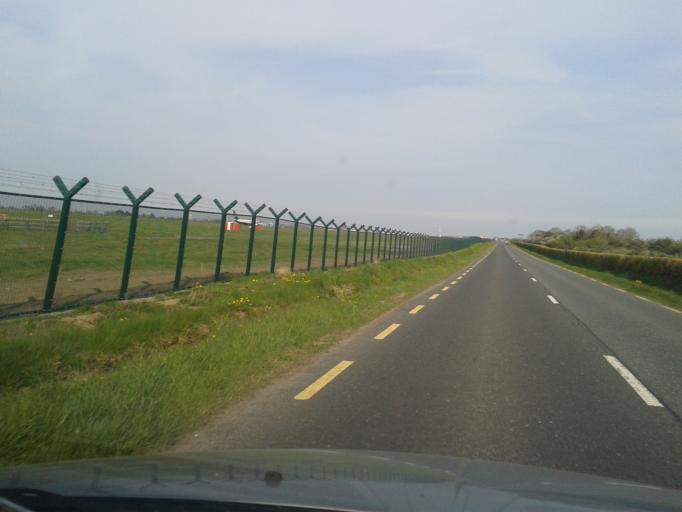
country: IE
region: Leinster
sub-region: Dublin City
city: Finglas
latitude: 53.4211
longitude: -6.2987
